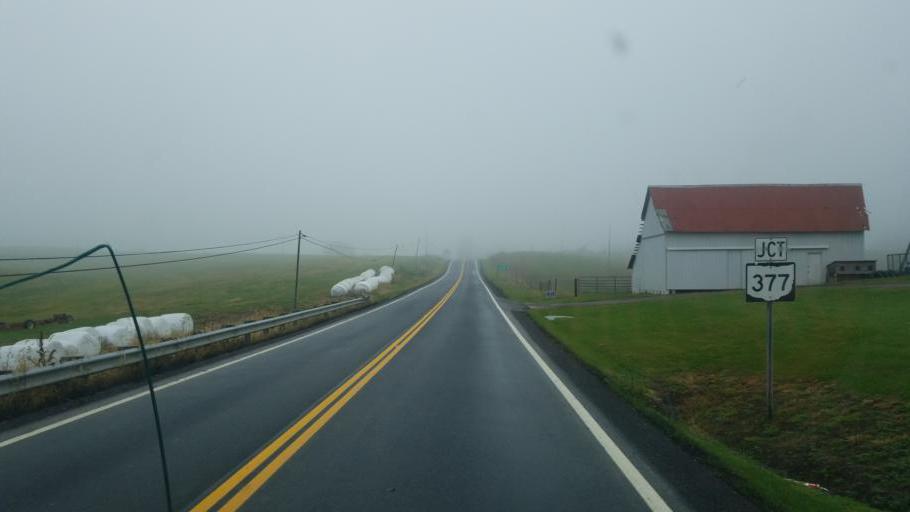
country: US
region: Ohio
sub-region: Morgan County
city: McConnelsville
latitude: 39.5676
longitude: -81.8450
